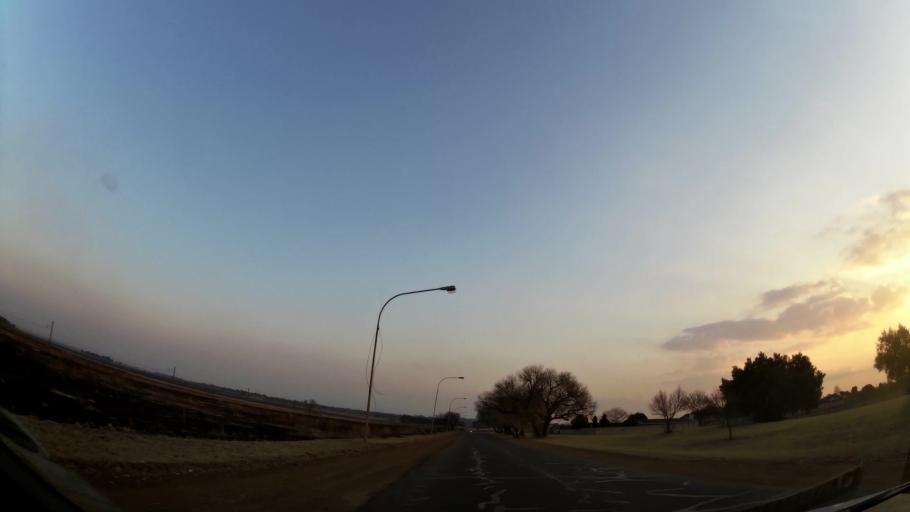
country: ZA
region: Gauteng
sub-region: Ekurhuleni Metropolitan Municipality
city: Springs
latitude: -26.3268
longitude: 28.4459
